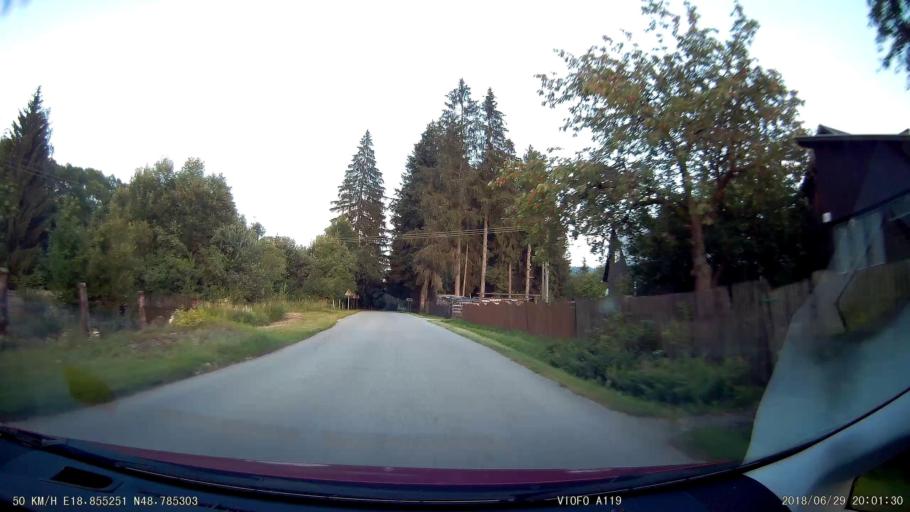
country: SK
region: Banskobystricky
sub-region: Okres Ziar nad Hronom
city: Kremnica
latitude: 48.7852
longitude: 18.8554
